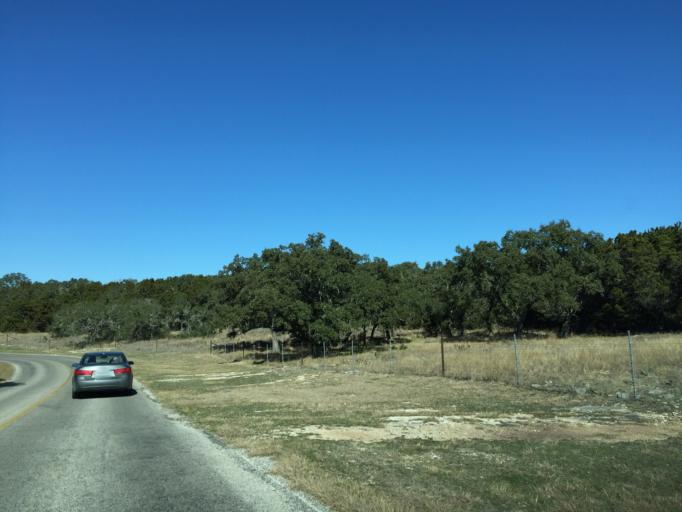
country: US
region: Texas
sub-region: Comal County
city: Garden Ridge
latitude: 29.6931
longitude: -98.3391
